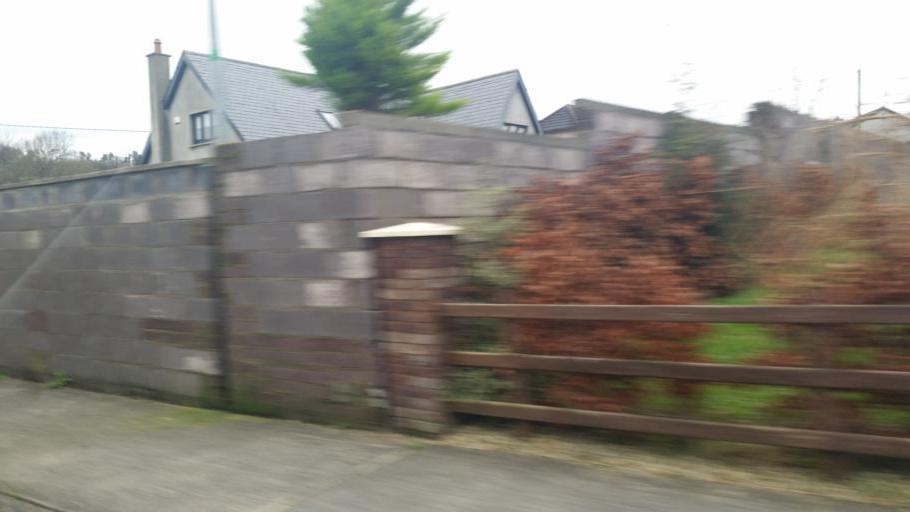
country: IE
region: Leinster
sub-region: An Mhi
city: Duleek
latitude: 53.6920
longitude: -6.4214
